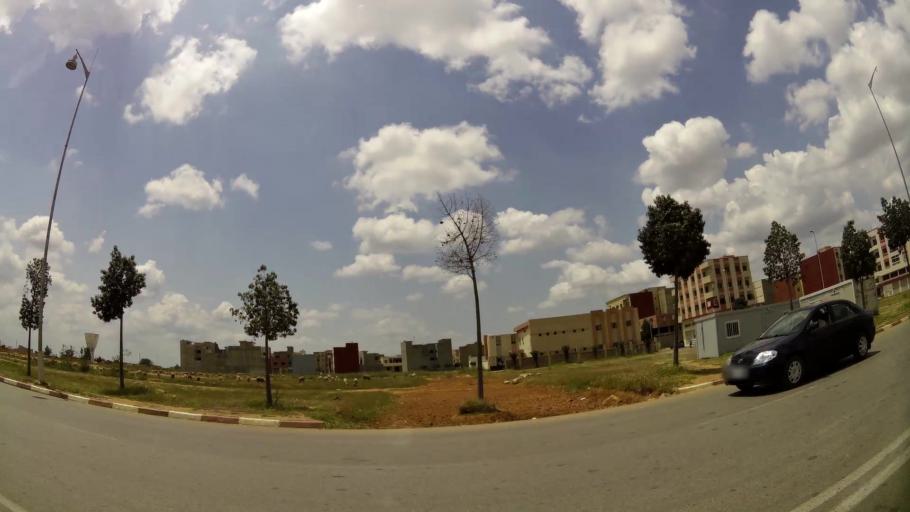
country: MA
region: Rabat-Sale-Zemmour-Zaer
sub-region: Khemisset
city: Tiflet
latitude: 34.0053
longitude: -6.5237
